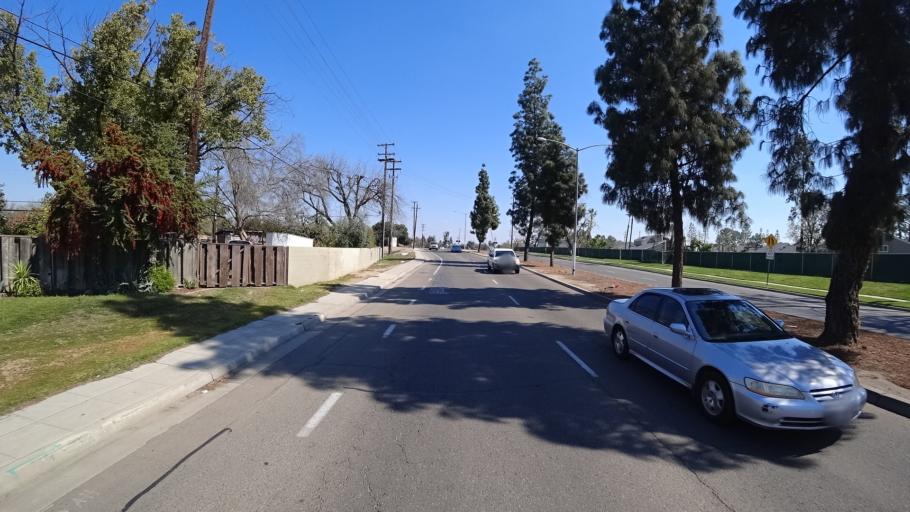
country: US
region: California
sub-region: Fresno County
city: Fresno
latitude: 36.7938
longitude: -119.8203
